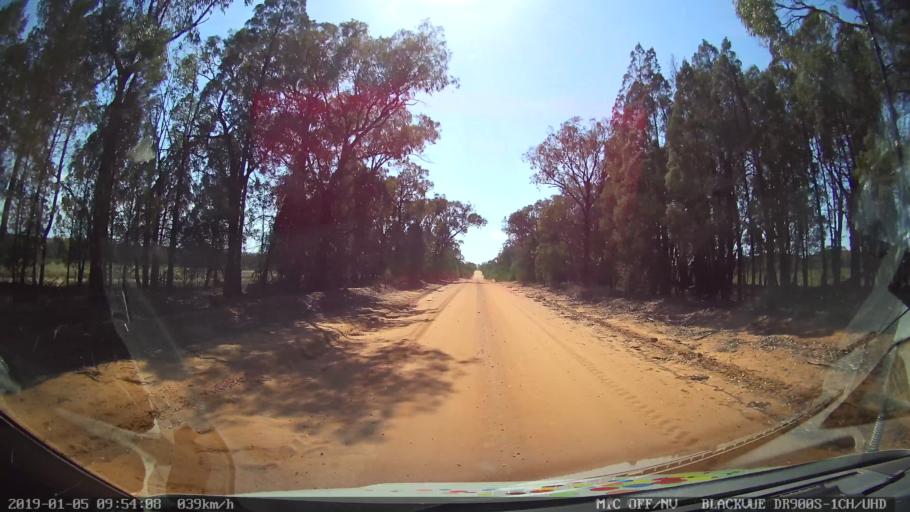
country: AU
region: New South Wales
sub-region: Gilgandra
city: Gilgandra
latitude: -31.6628
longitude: 148.7777
